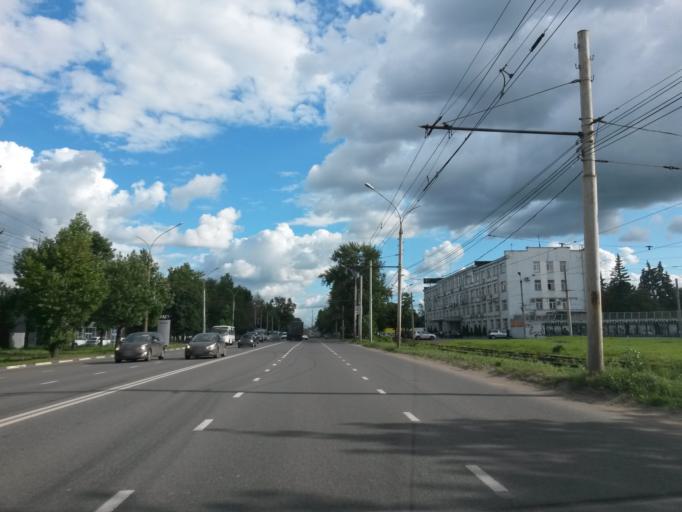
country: RU
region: Jaroslavl
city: Yaroslavl
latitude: 57.6492
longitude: 39.8487
